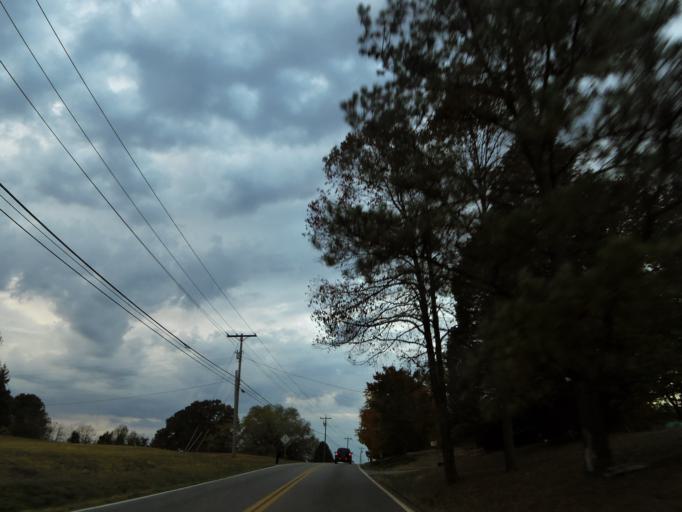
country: US
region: Tennessee
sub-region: Blount County
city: Louisville
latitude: 35.7776
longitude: -84.0256
